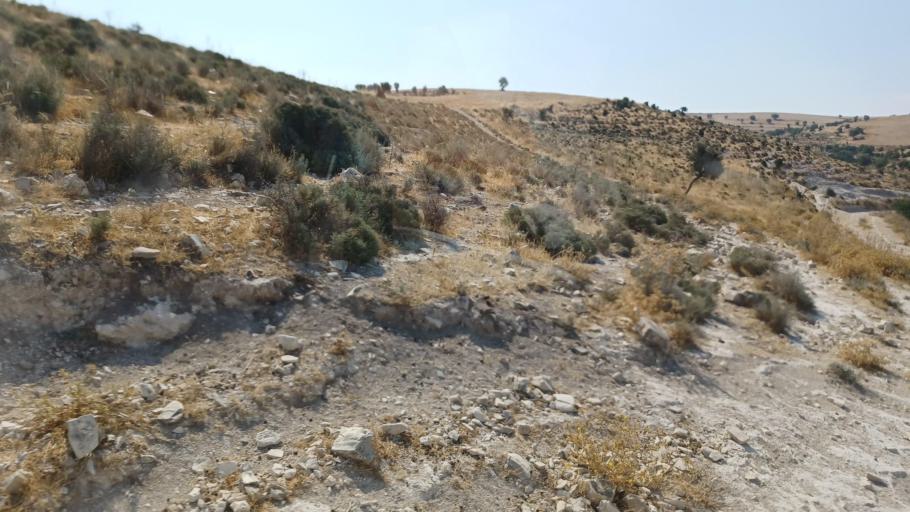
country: CY
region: Lefkosia
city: Lympia
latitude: 34.9821
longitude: 33.4794
